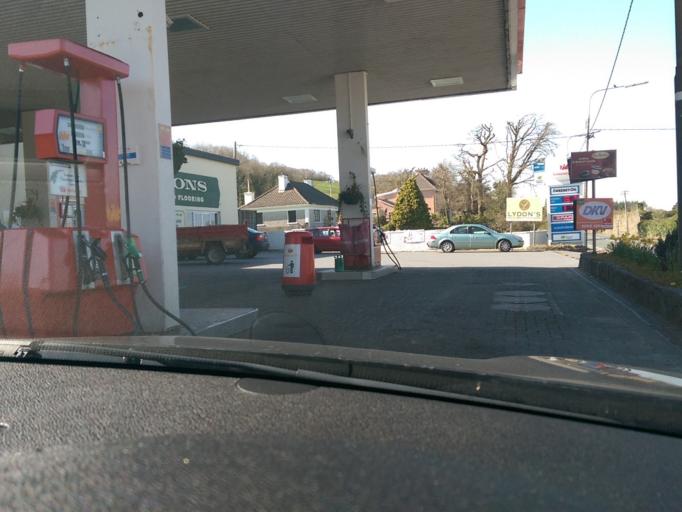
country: IE
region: Connaught
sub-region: County Galway
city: Moycullen
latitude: 53.3410
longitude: -9.1850
